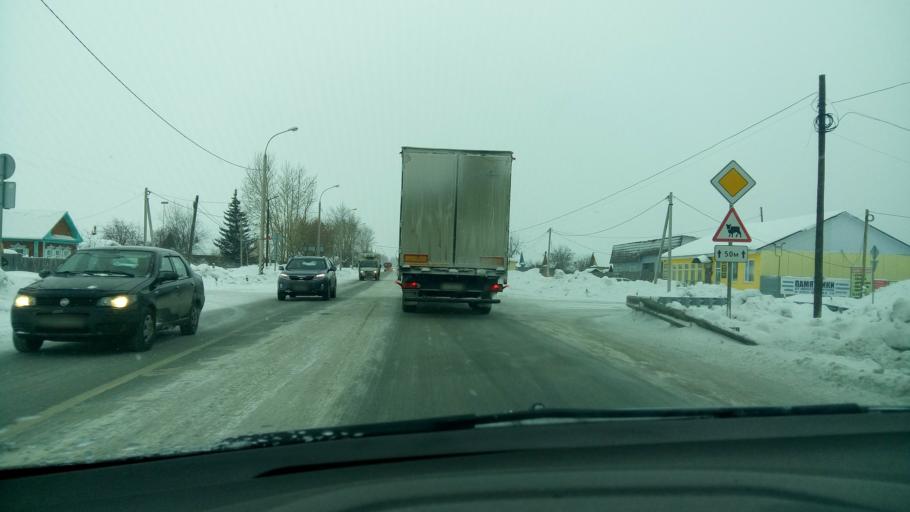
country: RU
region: Sverdlovsk
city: Zarechnyy
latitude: 56.7520
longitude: 61.3213
